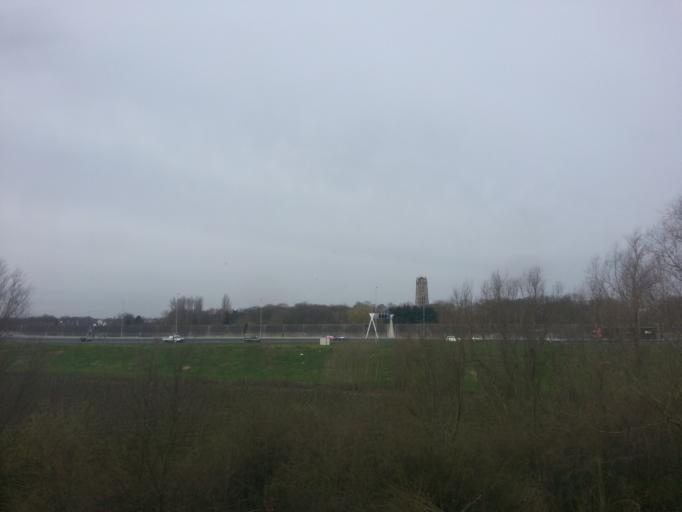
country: NL
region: Gelderland
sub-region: Gemeente Zaltbommel
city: Zaltbommel
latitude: 51.8115
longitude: 5.2627
